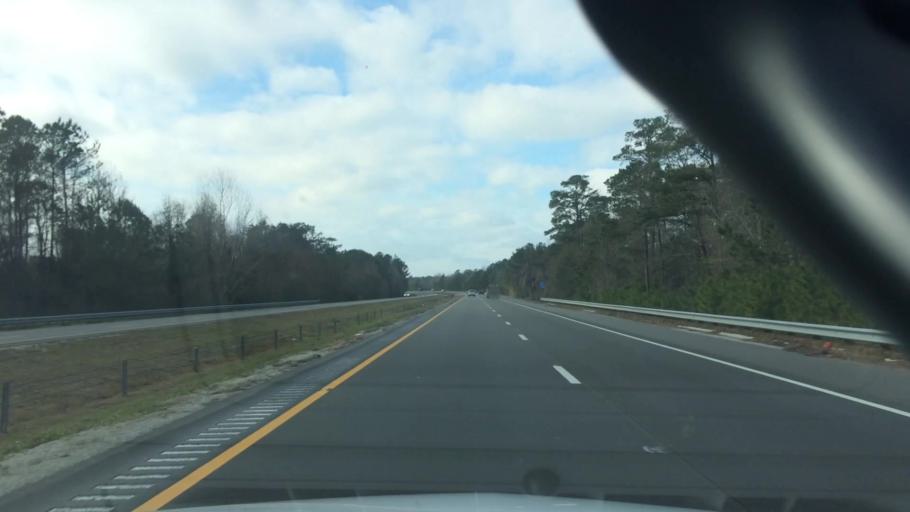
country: US
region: North Carolina
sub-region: New Hanover County
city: Wrightsboro
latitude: 34.3182
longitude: -77.9266
